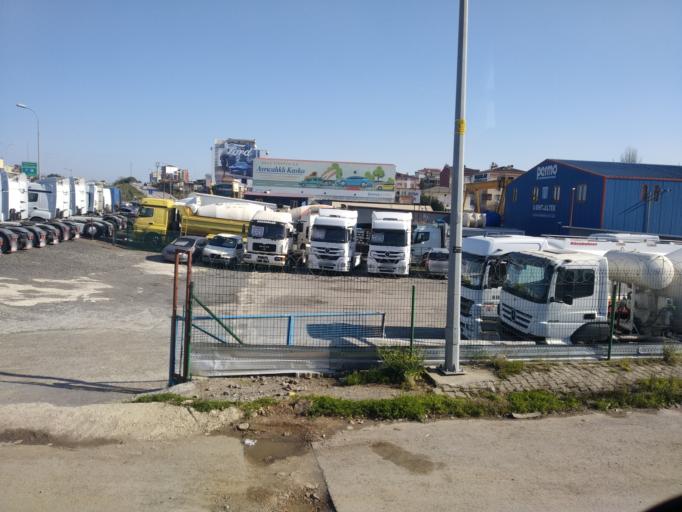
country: TR
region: Istanbul
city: Samandira
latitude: 40.9903
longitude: 29.1764
